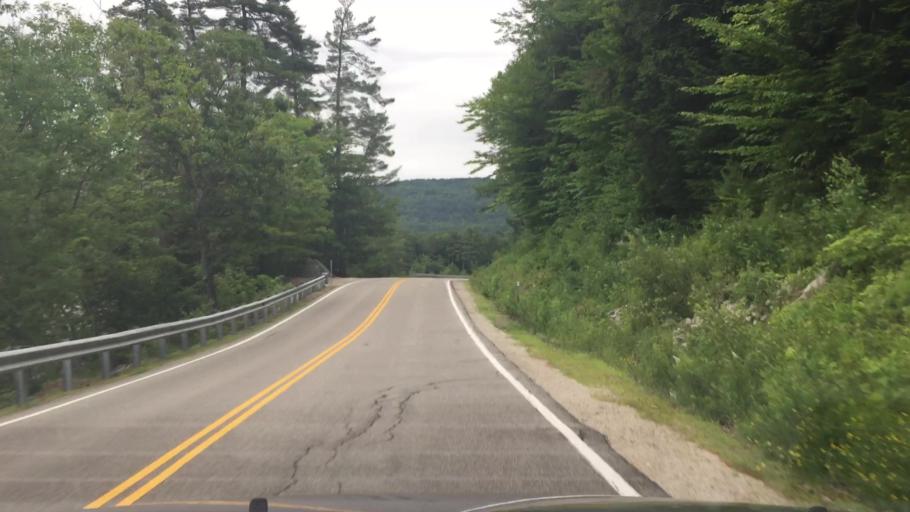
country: US
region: New Hampshire
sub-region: Carroll County
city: Madison
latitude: 43.9070
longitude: -71.0773
